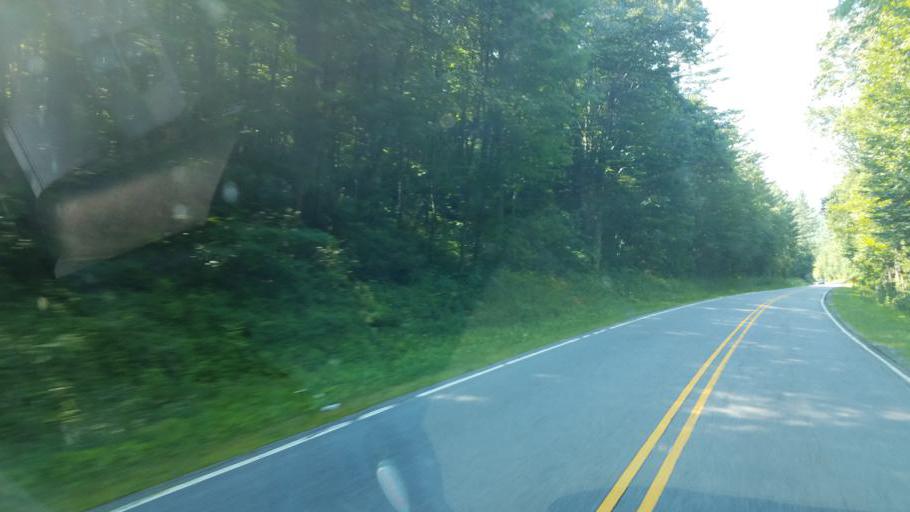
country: US
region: North Carolina
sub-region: Avery County
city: Newland
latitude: 35.9936
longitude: -81.8910
